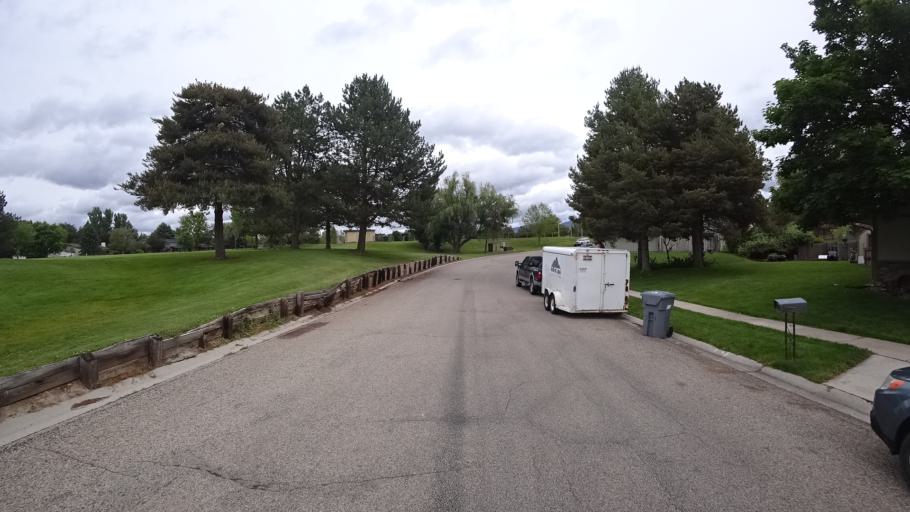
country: US
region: Idaho
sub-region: Ada County
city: Eagle
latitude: 43.6992
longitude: -116.3369
